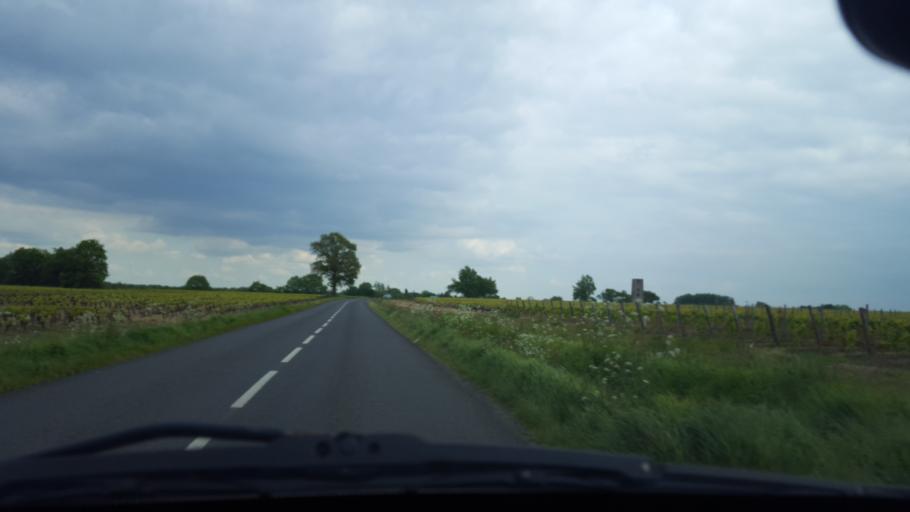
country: FR
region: Pays de la Loire
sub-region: Departement de la Loire-Atlantique
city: La Limouziniere
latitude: 46.9982
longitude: -1.6042
